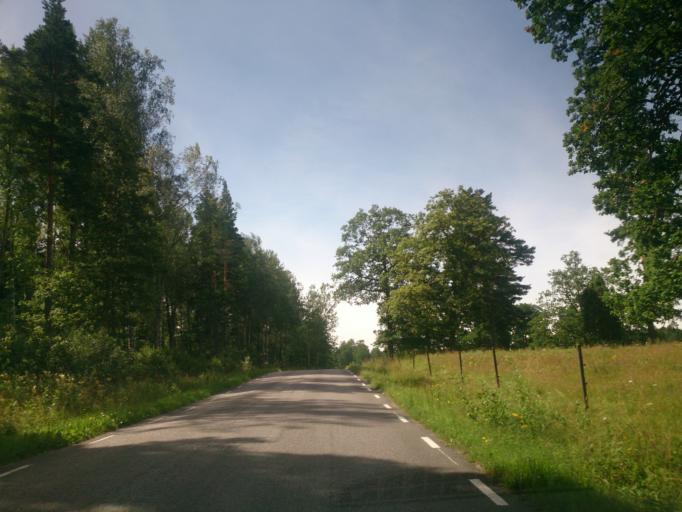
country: SE
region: OEstergoetland
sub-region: Valdemarsviks Kommun
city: Valdemarsvik
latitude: 58.3347
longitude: 16.6416
